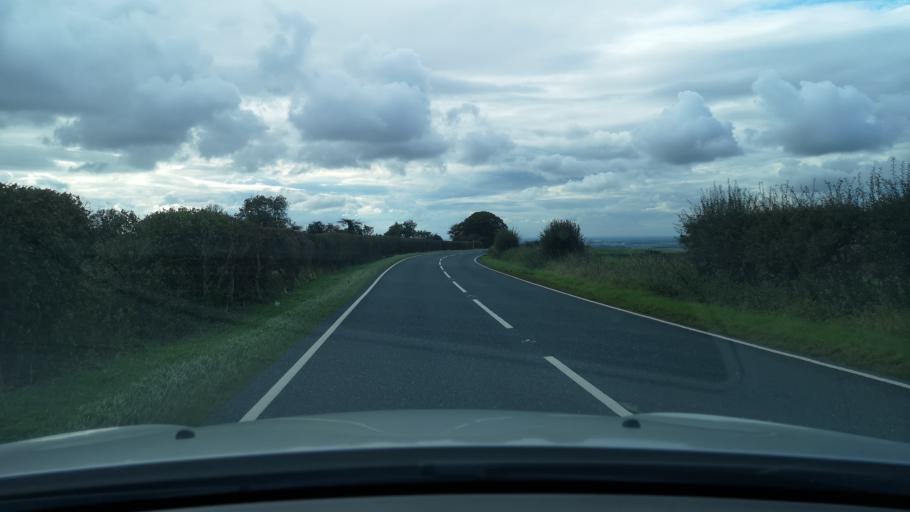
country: GB
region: England
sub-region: East Riding of Yorkshire
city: South Cave
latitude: 53.7962
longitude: -0.5936
